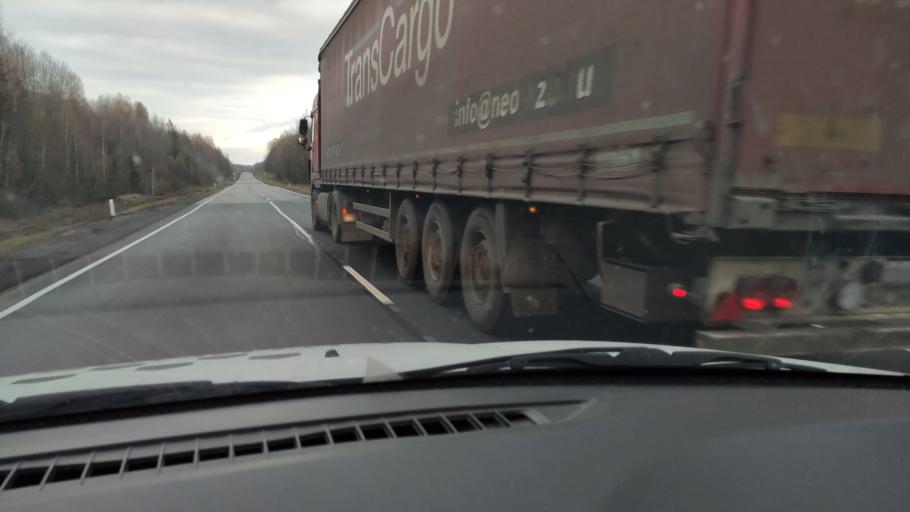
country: RU
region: Kirov
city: Omutninsk
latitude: 58.7601
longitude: 52.0129
